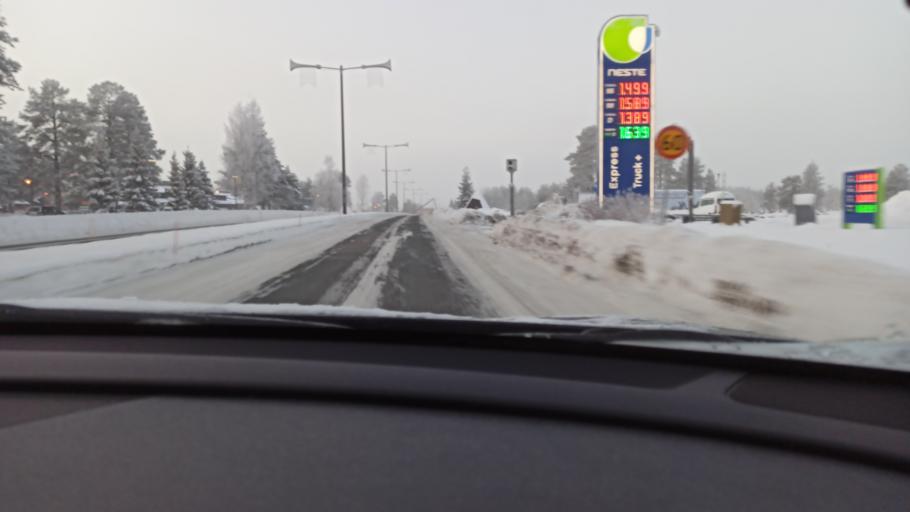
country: FI
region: Lapland
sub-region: Rovaniemi
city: Rovaniemi
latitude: 66.5452
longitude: 25.8514
